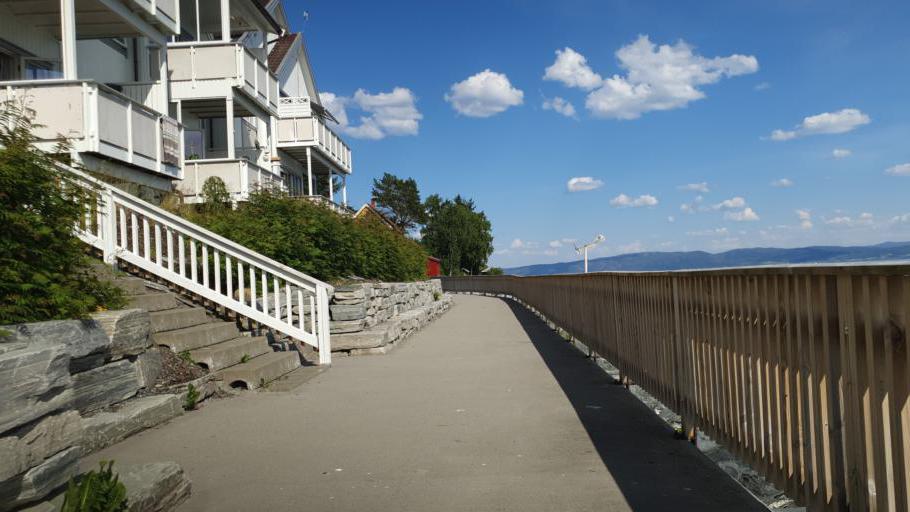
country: NO
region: Nord-Trondelag
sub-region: Leksvik
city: Leksvik
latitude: 63.6717
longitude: 10.6268
